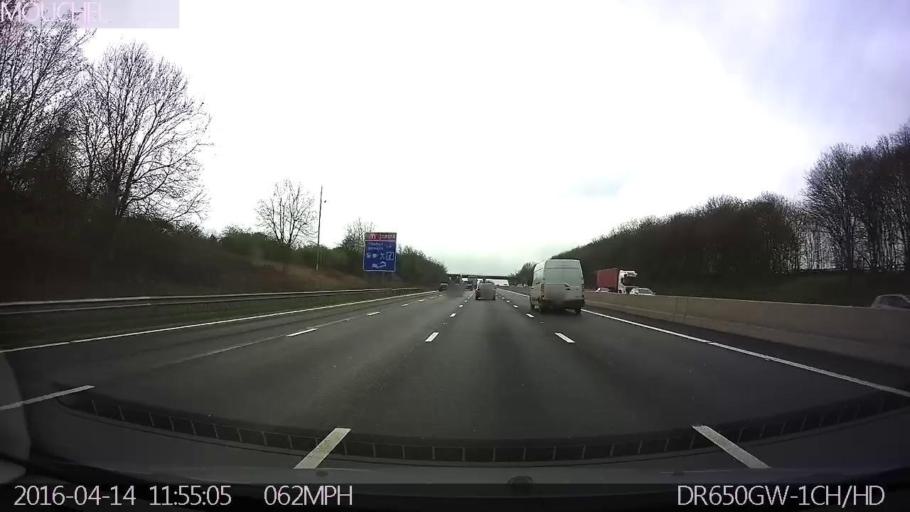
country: GB
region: England
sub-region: Derbyshire
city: Tibshelf
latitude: 53.1500
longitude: -1.3289
